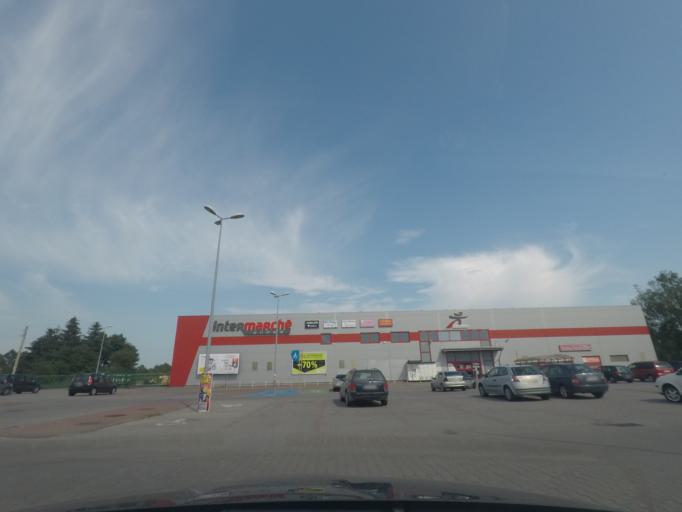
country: PL
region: Lesser Poland Voivodeship
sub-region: Powiat oswiecimski
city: Brzeszcze
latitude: 49.9742
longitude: 19.1450
